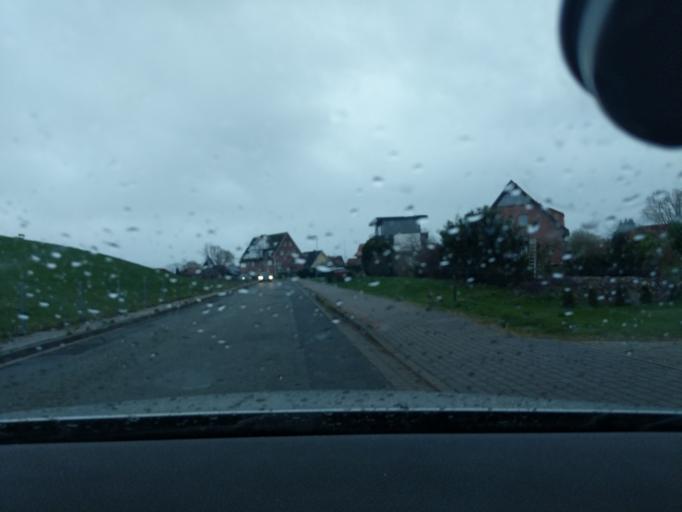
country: DE
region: Schleswig-Holstein
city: Haseldorf
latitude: 53.5943
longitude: 9.5687
